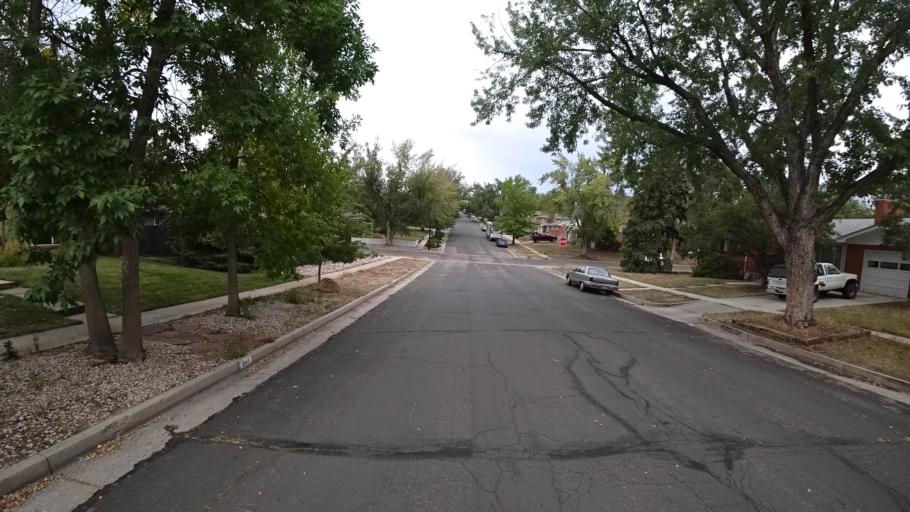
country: US
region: Colorado
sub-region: El Paso County
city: Colorado Springs
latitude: 38.8621
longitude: -104.7884
